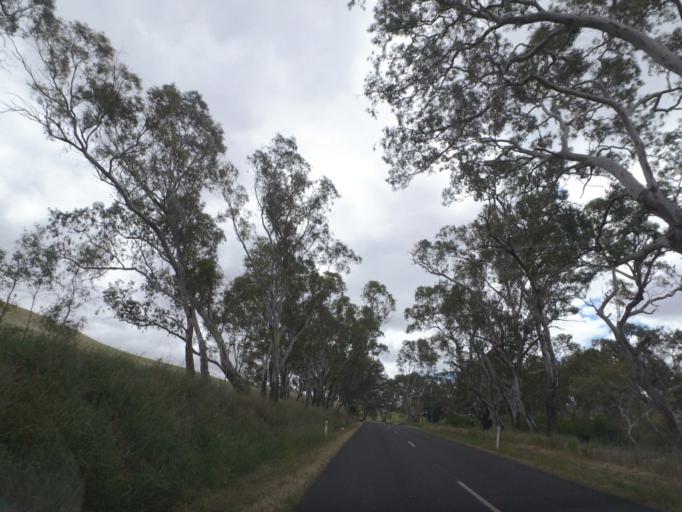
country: AU
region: Victoria
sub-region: Whittlesea
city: Whittlesea
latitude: -37.1921
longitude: 145.0385
